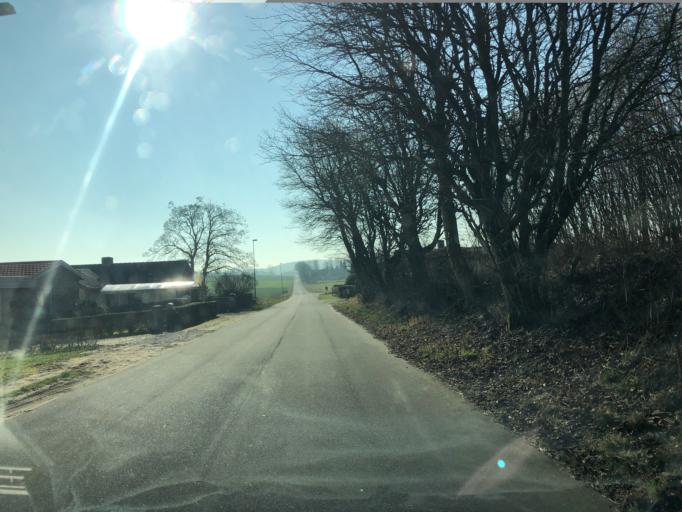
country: DK
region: Central Jutland
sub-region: Favrskov Kommune
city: Hammel
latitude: 56.2055
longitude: 9.8110
